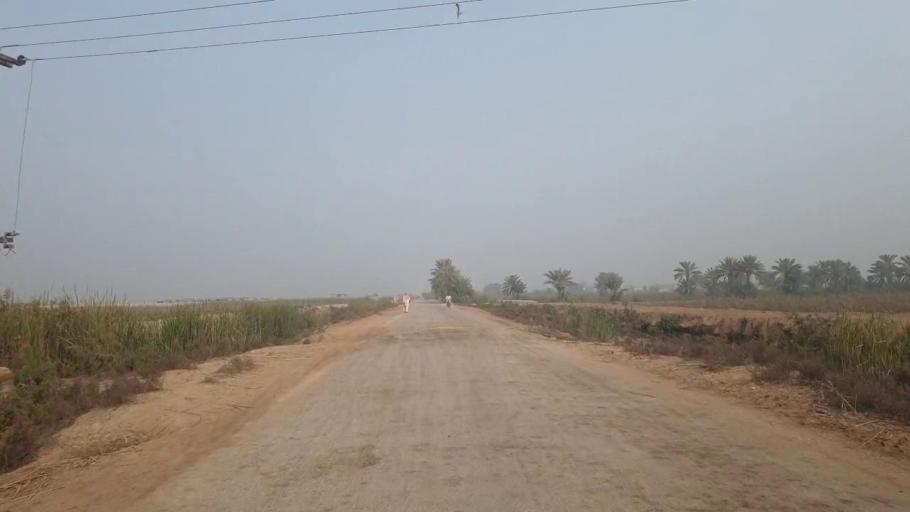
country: PK
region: Sindh
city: Tando Adam
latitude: 25.7944
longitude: 68.6103
